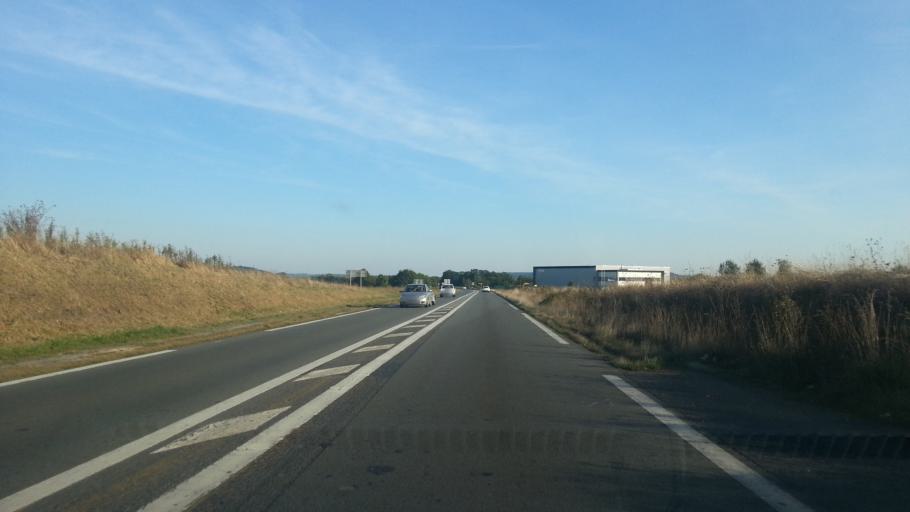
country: FR
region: Picardie
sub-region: Departement de l'Oise
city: Allonne
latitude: 49.4302
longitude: 2.1251
